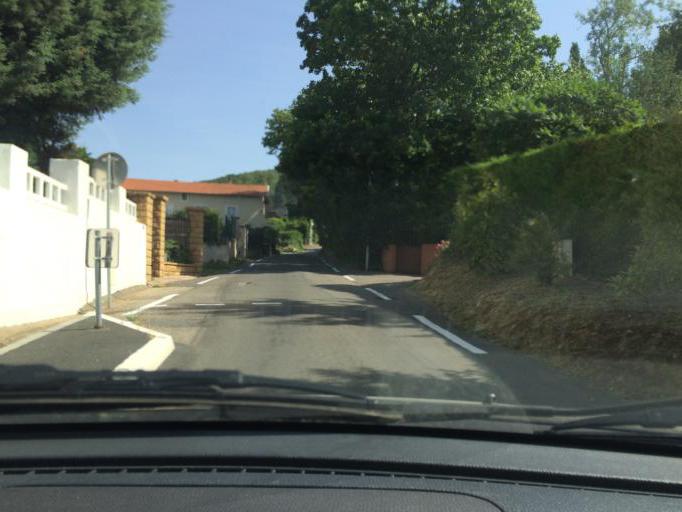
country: FR
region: Rhone-Alpes
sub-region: Departement du Rhone
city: Limonest
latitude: 45.8284
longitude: 4.7811
